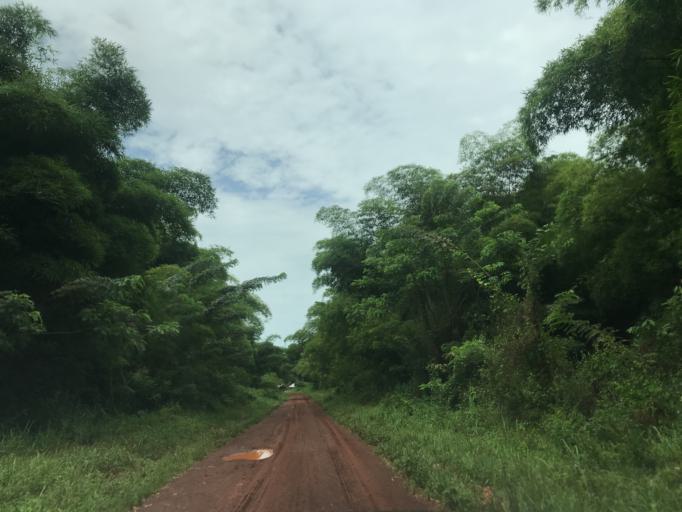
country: CD
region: Eastern Province
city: Buta
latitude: 2.4327
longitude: 24.8734
